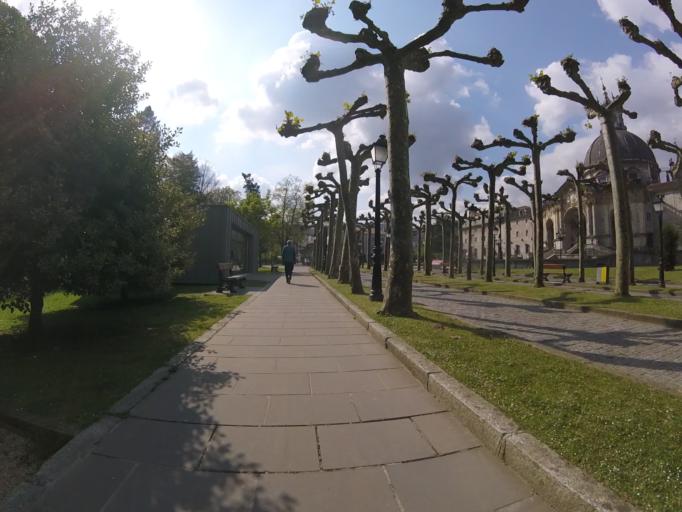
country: ES
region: Basque Country
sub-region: Provincia de Guipuzcoa
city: Azpeitia
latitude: 43.1753
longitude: -2.2820
